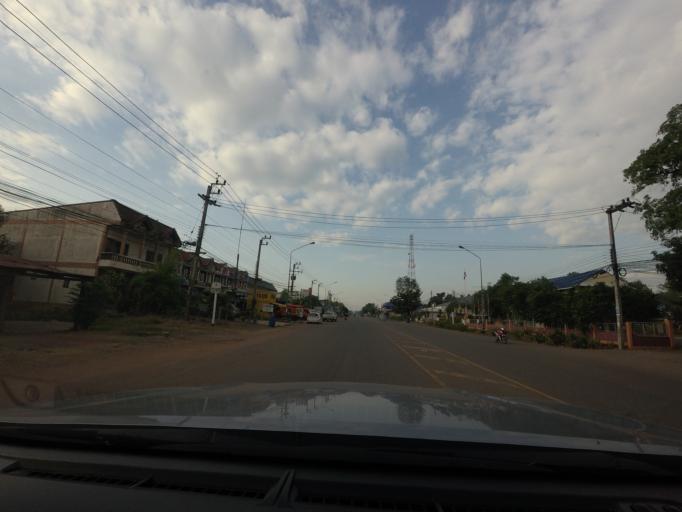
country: TH
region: Phitsanulok
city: Noen Maprang
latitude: 16.5685
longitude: 100.6346
